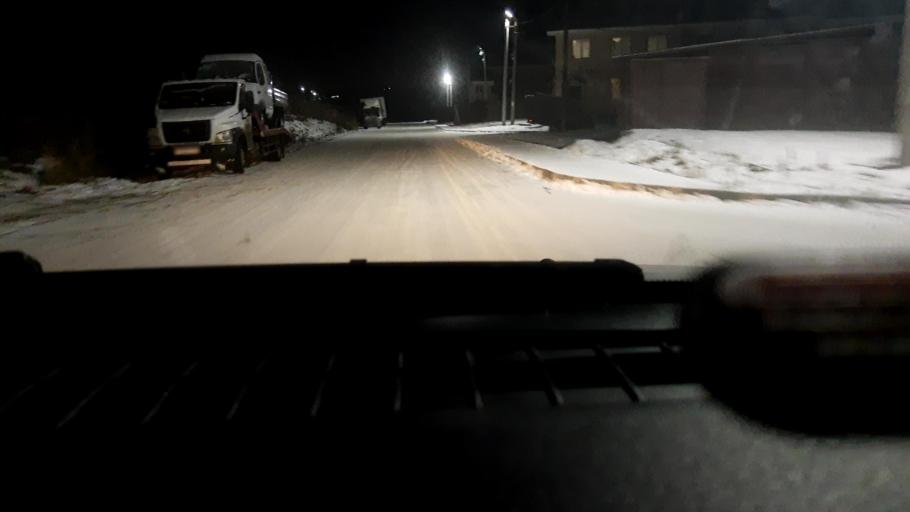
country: RU
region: Nizjnij Novgorod
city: Burevestnik
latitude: 56.1952
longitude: 43.8819
